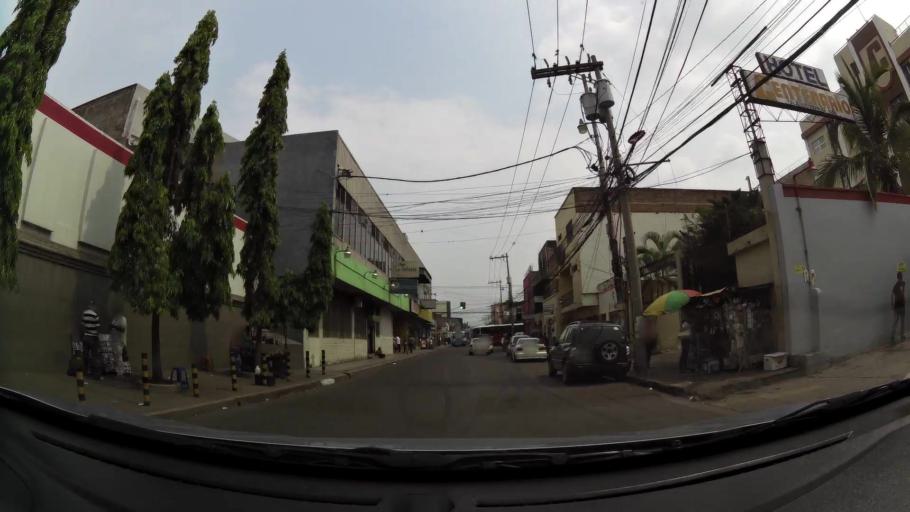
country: HN
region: Francisco Morazan
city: Tegucigalpa
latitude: 14.0961
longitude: -87.2100
